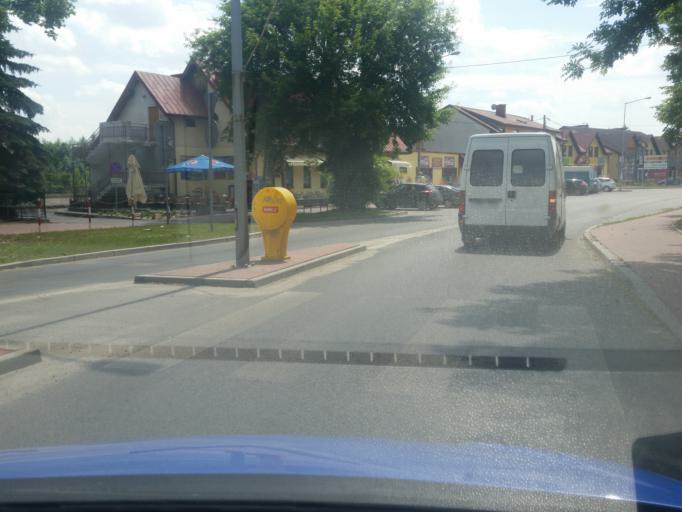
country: PL
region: Swietokrzyskie
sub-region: Powiat kazimierski
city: Kazimierza Wielka
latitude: 50.2653
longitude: 20.4934
